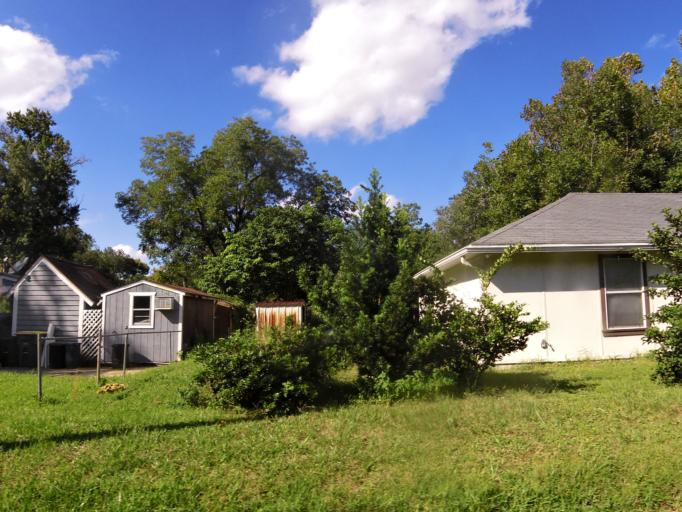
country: US
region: Florida
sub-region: Duval County
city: Jacksonville
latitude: 30.2744
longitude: -81.6323
